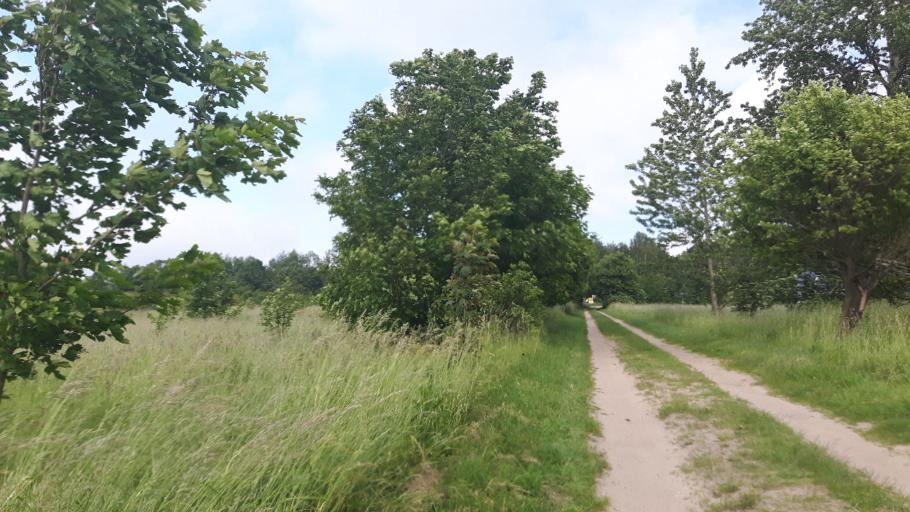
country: PL
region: Pomeranian Voivodeship
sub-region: Slupsk
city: Slupsk
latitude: 54.6001
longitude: 17.0098
